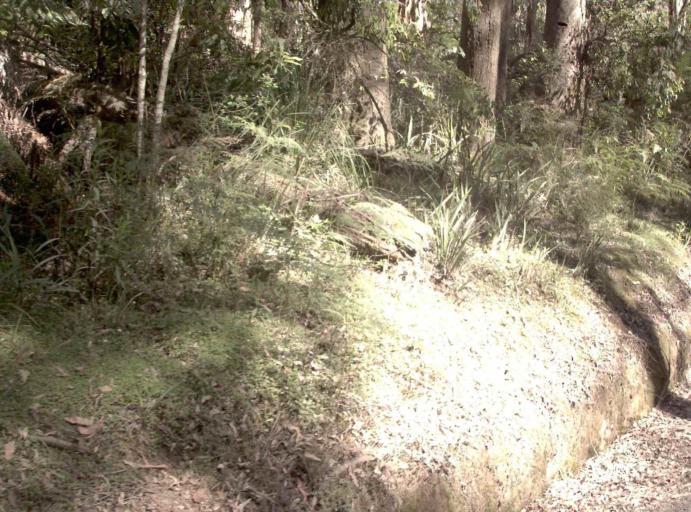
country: AU
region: New South Wales
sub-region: Bombala
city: Bombala
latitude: -37.2393
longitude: 148.7567
